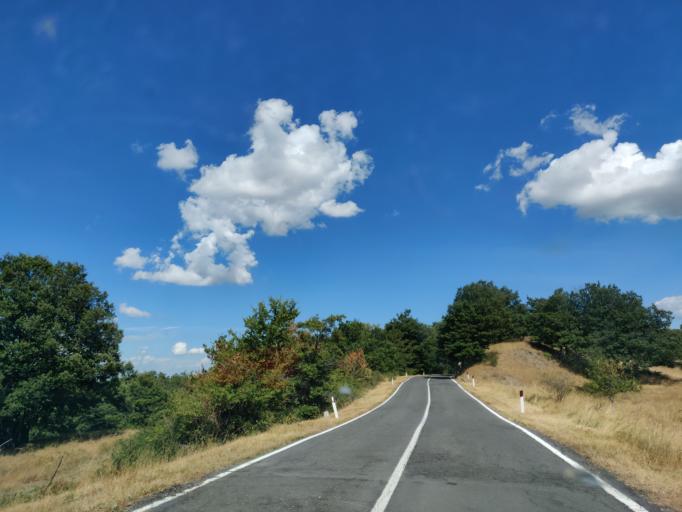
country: IT
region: Tuscany
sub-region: Provincia di Siena
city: Abbadia San Salvatore
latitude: 42.9102
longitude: 11.6875
